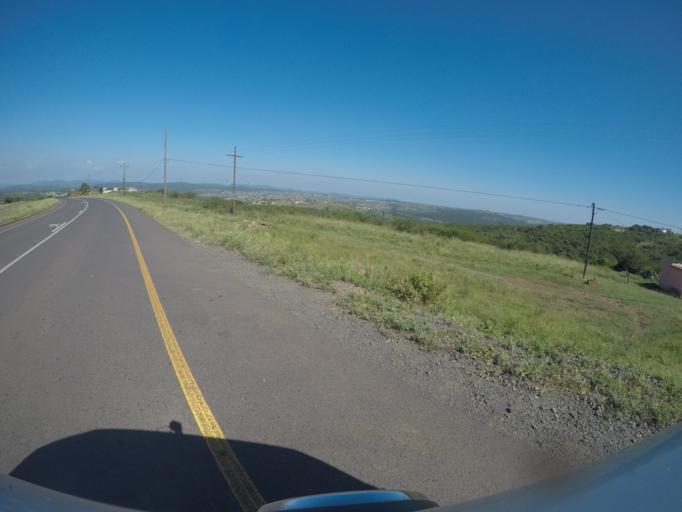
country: ZA
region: KwaZulu-Natal
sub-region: uThungulu District Municipality
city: Empangeni
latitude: -28.5709
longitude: 31.7123
